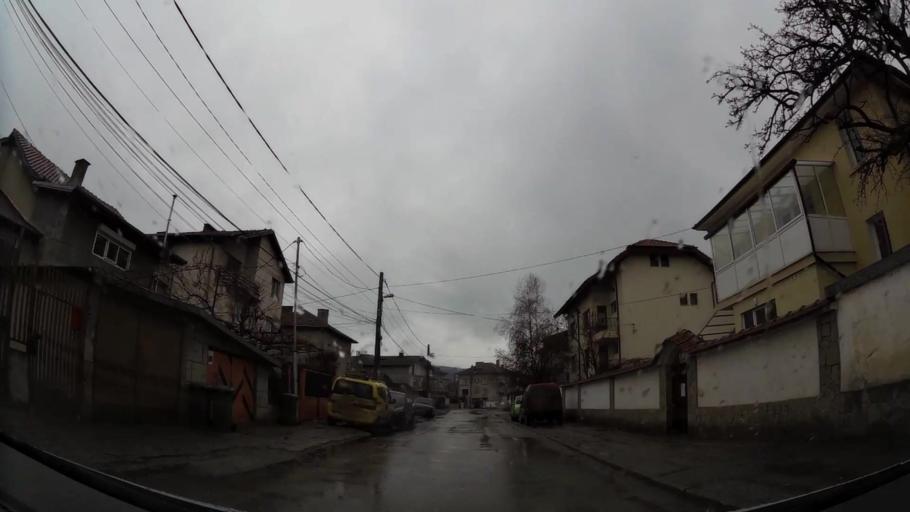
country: BG
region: Sofia-Capital
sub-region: Stolichna Obshtina
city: Sofia
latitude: 42.6285
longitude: 23.4126
